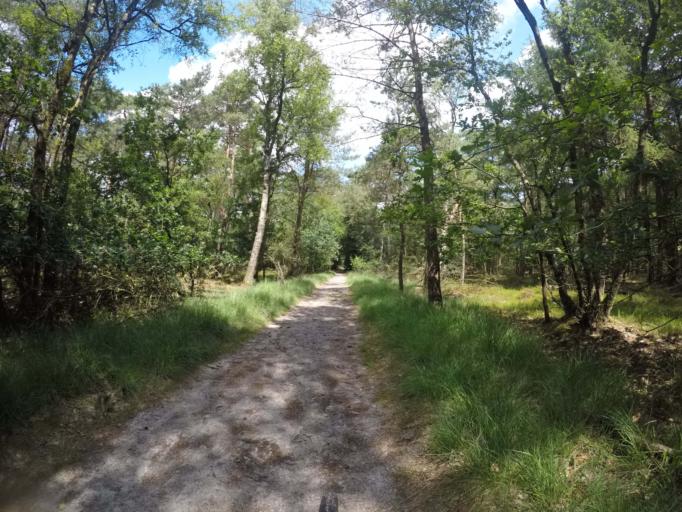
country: NL
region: Drenthe
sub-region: Gemeente Westerveld
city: Dwingeloo
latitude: 52.8721
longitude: 6.3098
